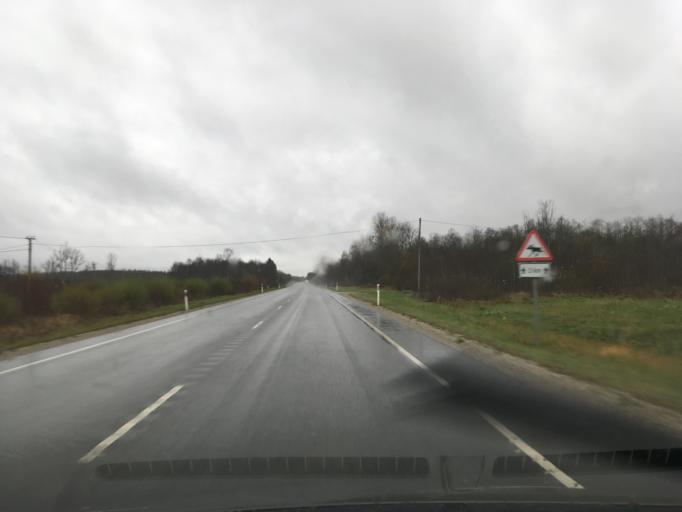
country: EE
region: Laeaene
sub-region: Lihula vald
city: Lihula
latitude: 58.8087
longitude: 24.0501
